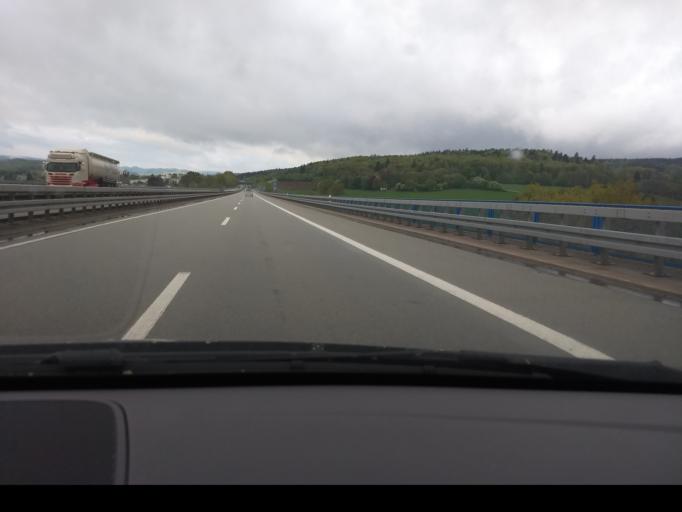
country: DE
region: North Rhine-Westphalia
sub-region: Regierungsbezirk Arnsberg
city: Meschede
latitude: 51.3662
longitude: 8.3096
